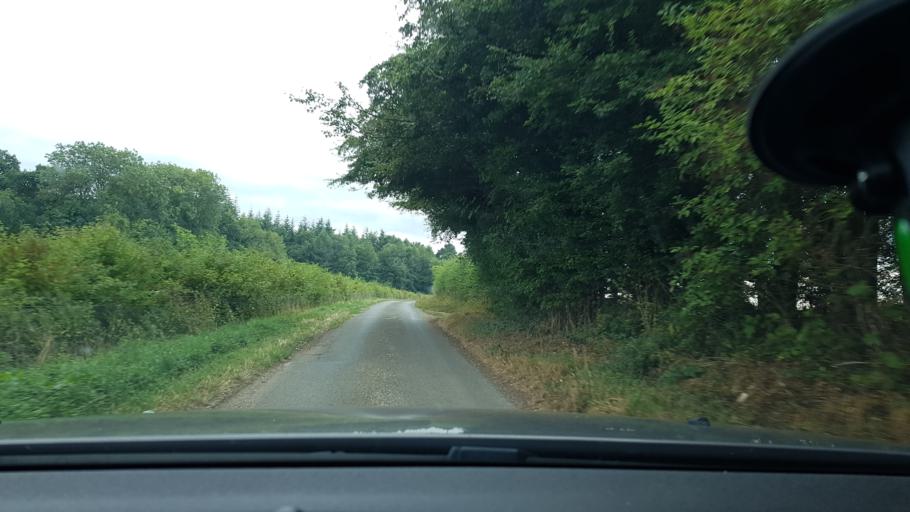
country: GB
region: England
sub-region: Wiltshire
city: Chilton Foliat
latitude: 51.4537
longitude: -1.5663
